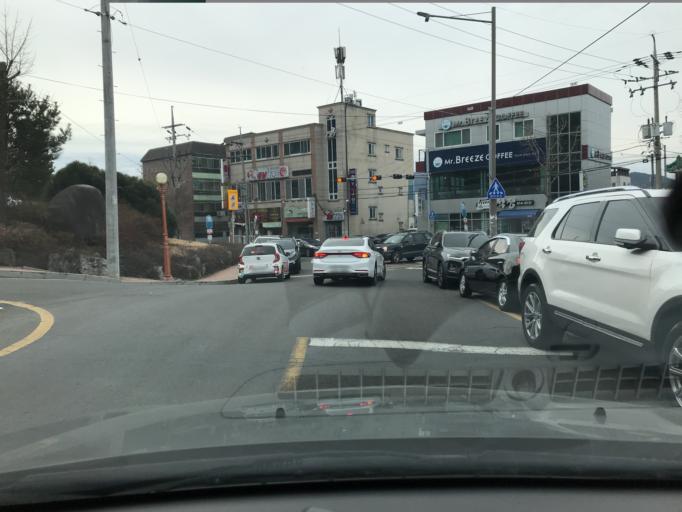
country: KR
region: Daegu
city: Hwawon
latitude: 35.6986
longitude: 128.4508
